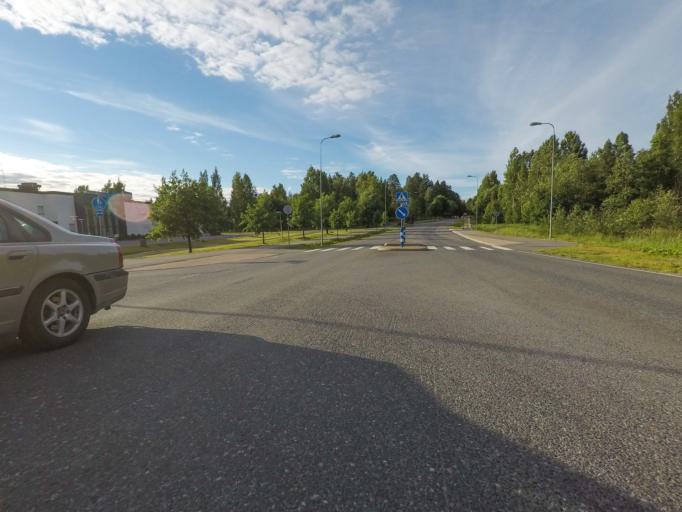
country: FI
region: Northern Savo
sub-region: Kuopio
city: Kuopio
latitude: 62.9744
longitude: 27.7026
